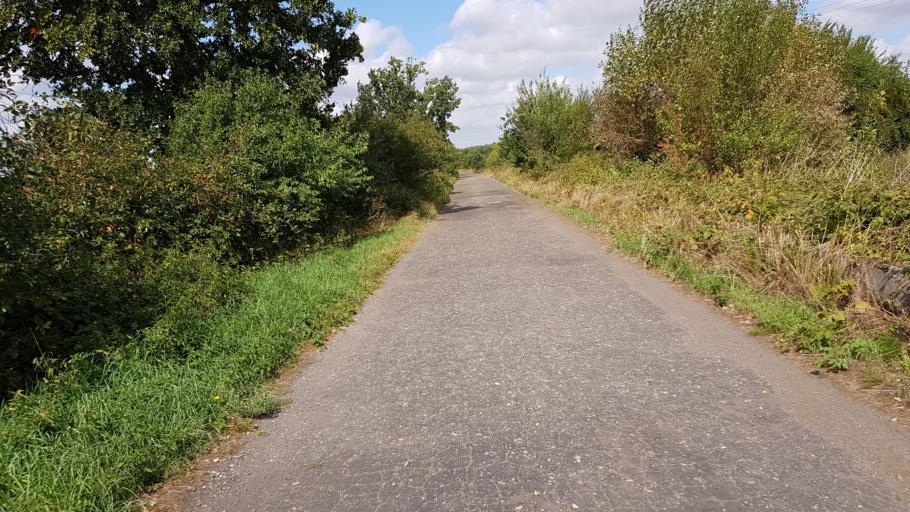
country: PL
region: West Pomeranian Voivodeship
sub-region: Powiat choszczenski
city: Krzecin
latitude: 52.9791
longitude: 15.4906
